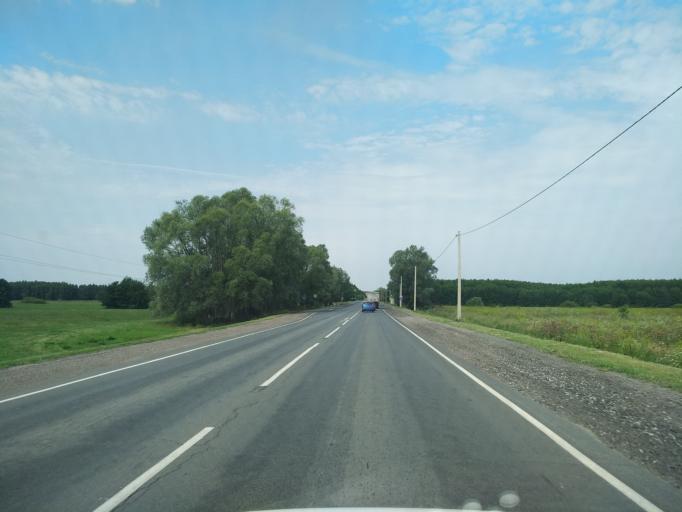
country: RU
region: Voronezj
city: Orlovo
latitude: 51.6806
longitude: 39.6034
